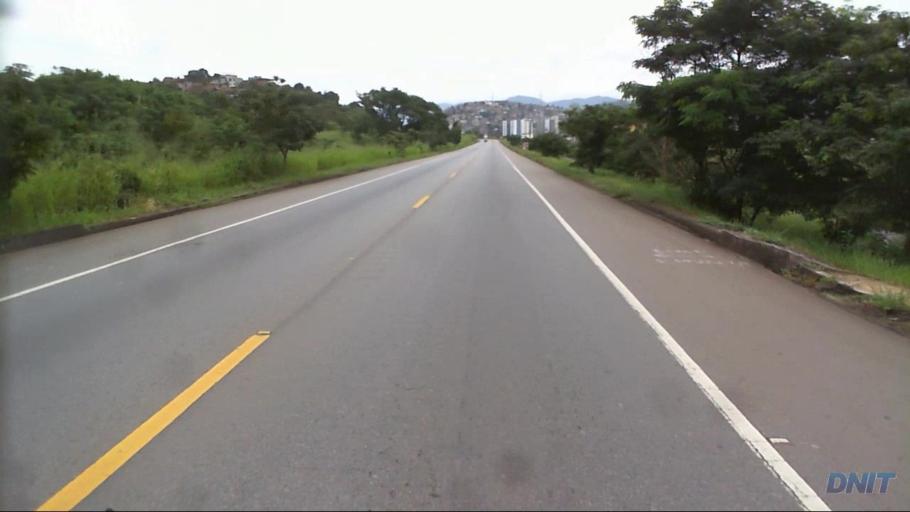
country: BR
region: Minas Gerais
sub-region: Coronel Fabriciano
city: Coronel Fabriciano
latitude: -19.5301
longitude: -42.6110
